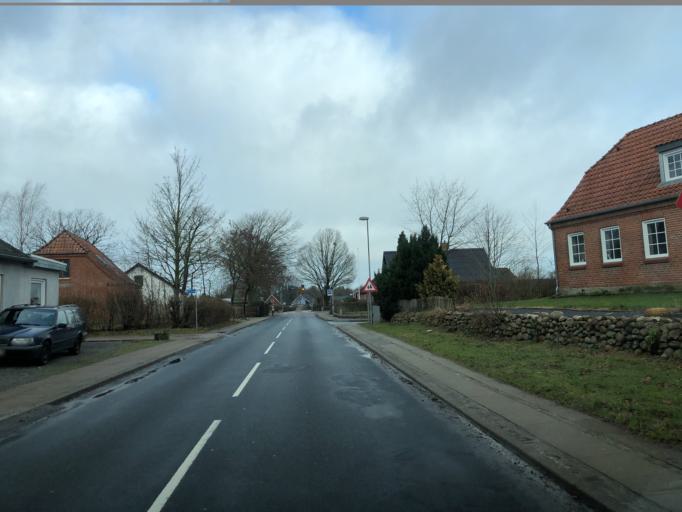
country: DK
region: Central Jutland
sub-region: Skive Kommune
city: Skive
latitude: 56.4441
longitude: 9.0061
